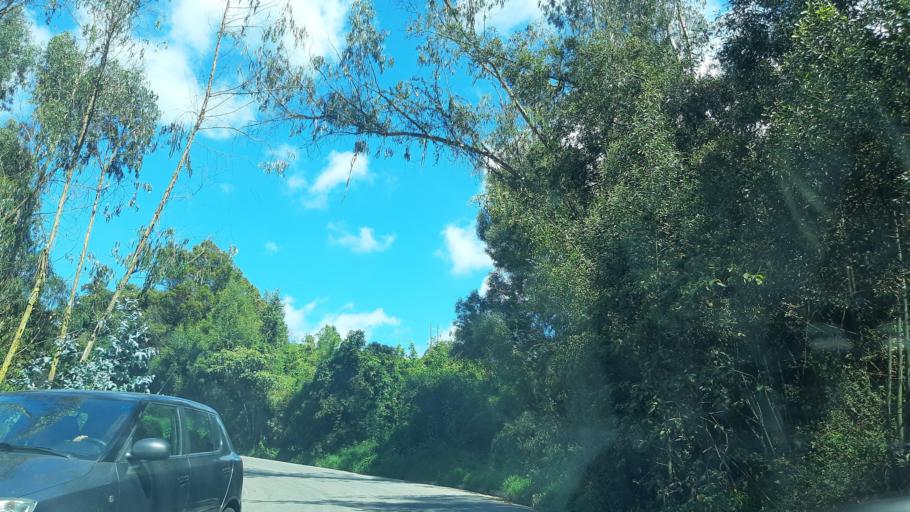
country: CO
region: Boyaca
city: Samaca
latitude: 5.4813
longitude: -73.4700
